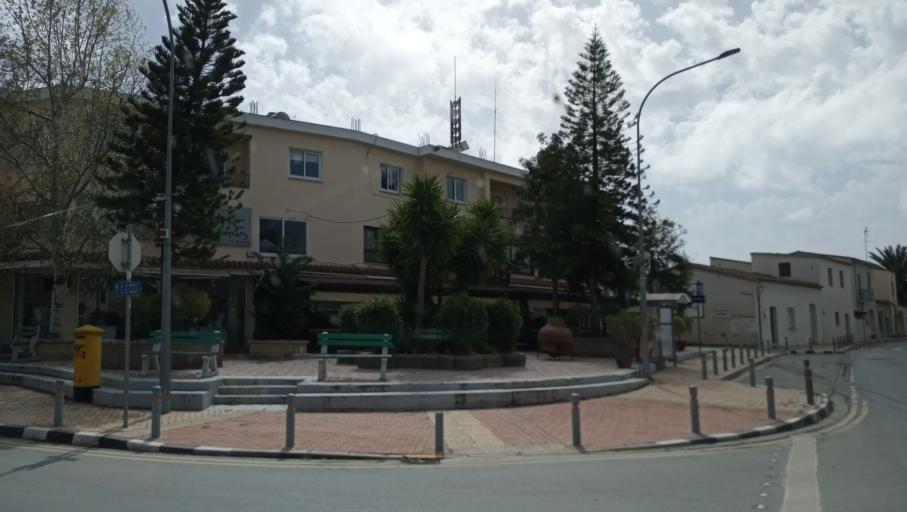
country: CY
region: Lefkosia
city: Dali
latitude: 35.0218
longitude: 33.4194
